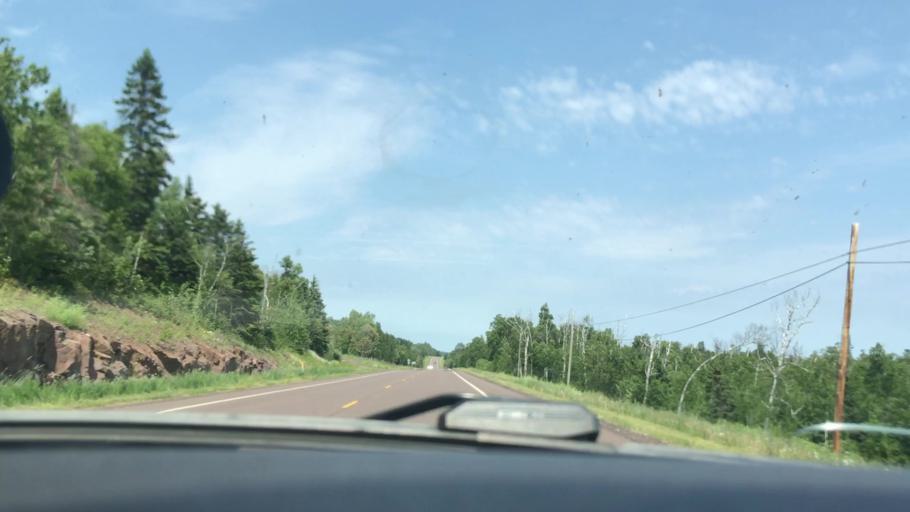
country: US
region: Minnesota
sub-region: Lake County
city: Silver Bay
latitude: 47.4393
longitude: -91.0754
